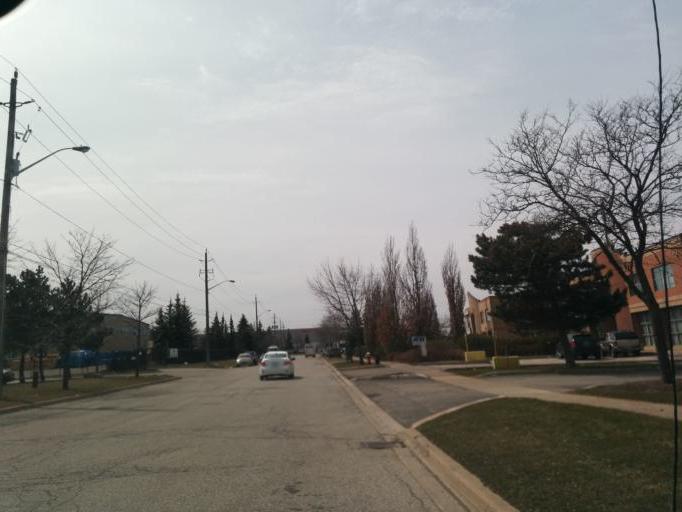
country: CA
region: Ontario
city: Brampton
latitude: 43.7134
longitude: -79.8013
